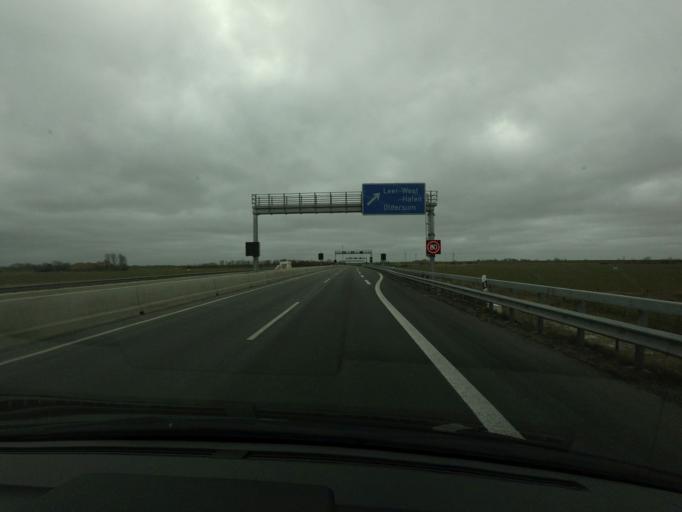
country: DE
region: Lower Saxony
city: Jemgum
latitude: 53.2405
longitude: 7.4165
